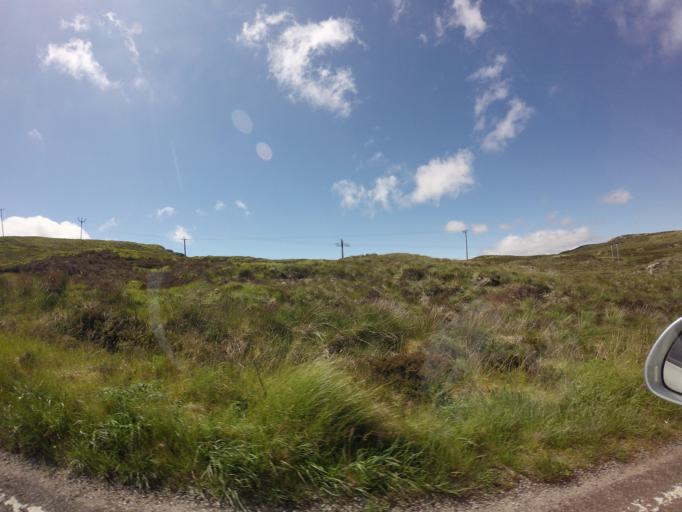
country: GB
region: Scotland
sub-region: Eilean Siar
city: Stornoway
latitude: 58.1444
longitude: -6.5090
